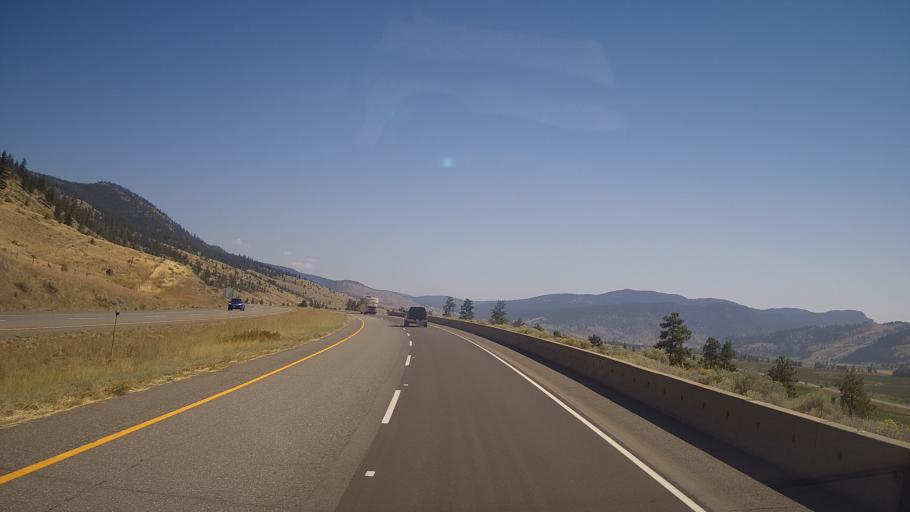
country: CA
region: British Columbia
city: Merritt
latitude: 50.1289
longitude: -120.7434
